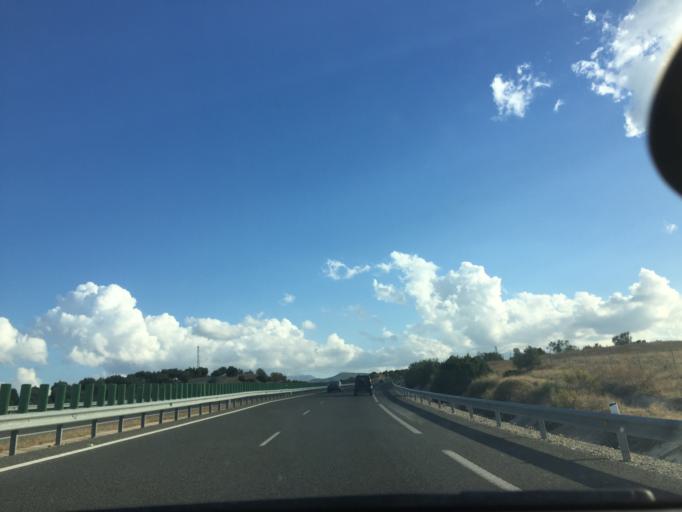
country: ES
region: Andalusia
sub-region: Provincia de Jaen
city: Jaen
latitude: 37.8134
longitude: -3.7351
